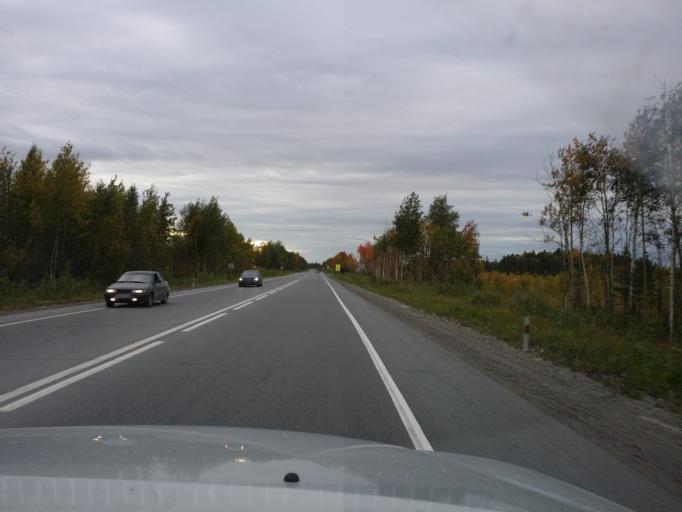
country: RU
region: Khanty-Mansiyskiy Avtonomnyy Okrug
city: Megion
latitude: 61.0691
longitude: 76.2403
